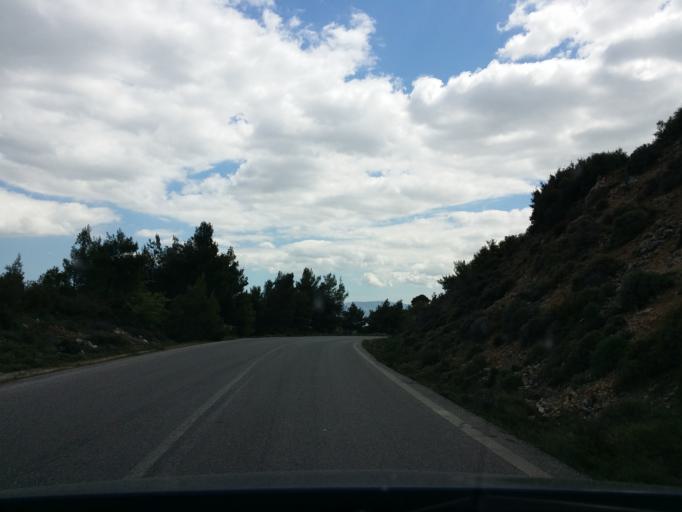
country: GR
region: Attica
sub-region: Nomarchia Dytikis Attikis
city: Fyli
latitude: 38.1205
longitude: 23.6506
